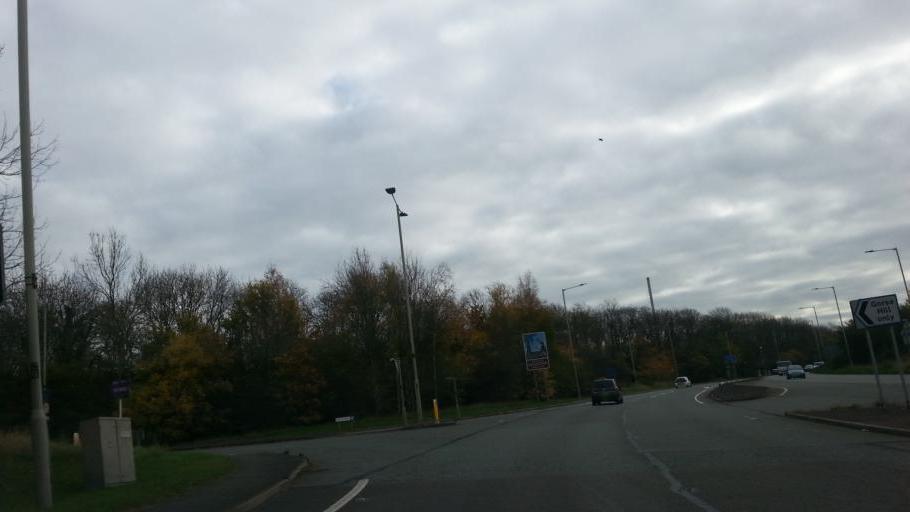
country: GB
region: England
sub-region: Leicestershire
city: Anstey
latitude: 52.6649
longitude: -1.1780
